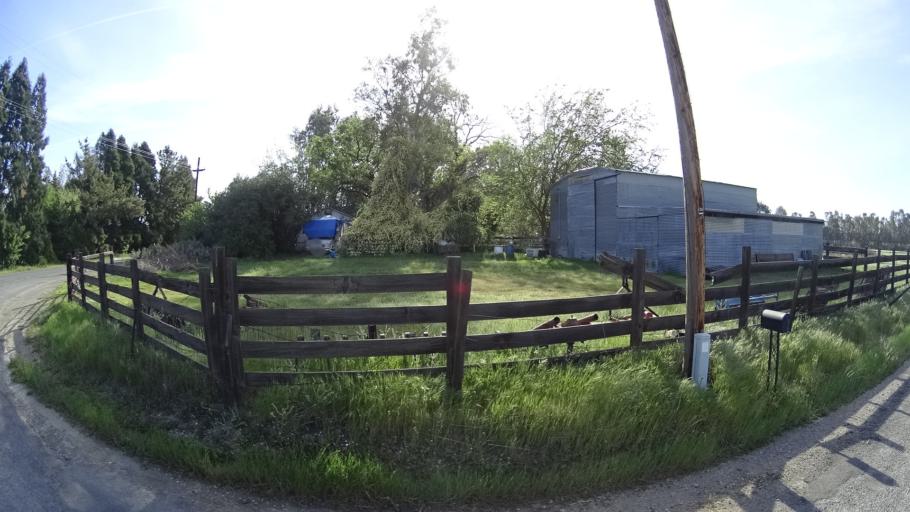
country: US
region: California
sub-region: Glenn County
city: Orland
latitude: 39.7223
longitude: -122.2159
